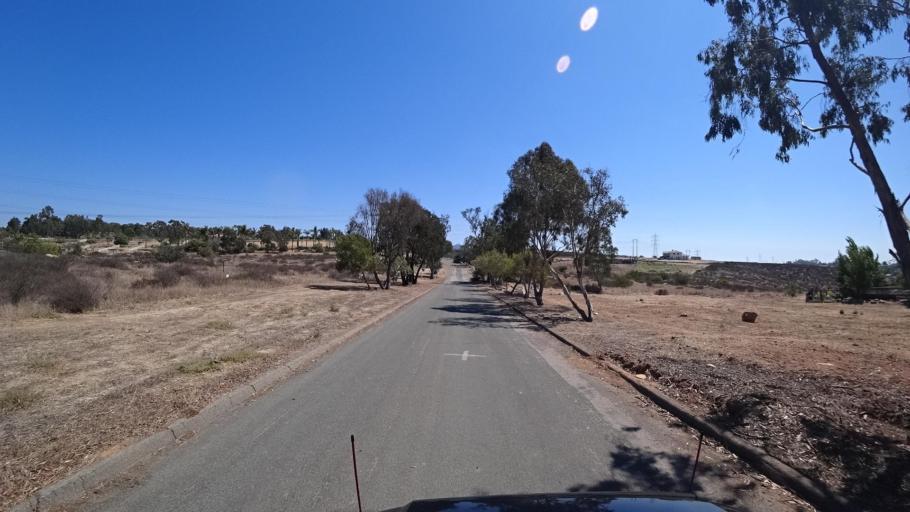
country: US
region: California
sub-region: San Diego County
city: Fairbanks Ranch
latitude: 33.0192
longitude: -117.1708
